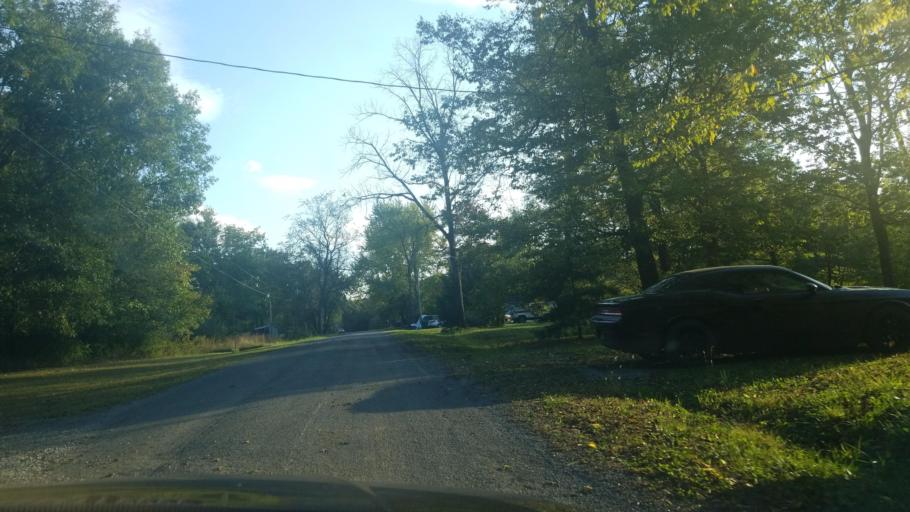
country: US
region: Illinois
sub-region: Williamson County
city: Marion
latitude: 37.7641
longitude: -88.8070
